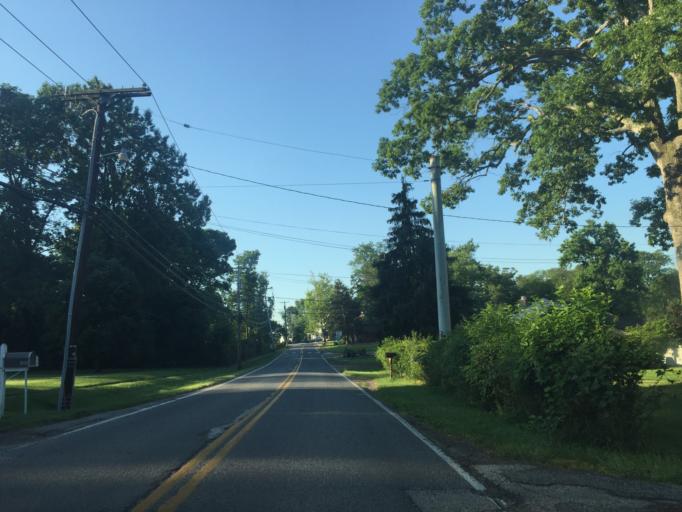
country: US
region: Maryland
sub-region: Howard County
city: Elkridge
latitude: 39.2289
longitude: -76.7072
